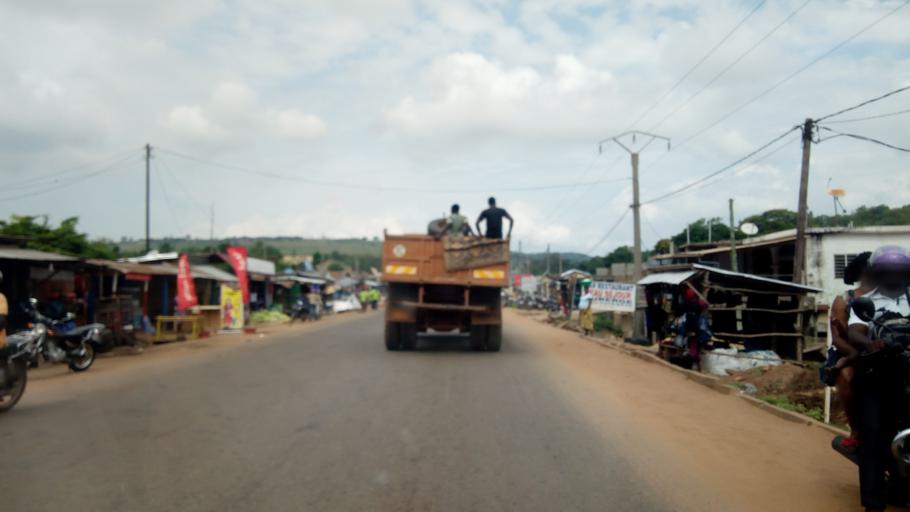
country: TG
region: Plateaux
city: Atakpame
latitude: 7.5166
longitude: 1.1491
